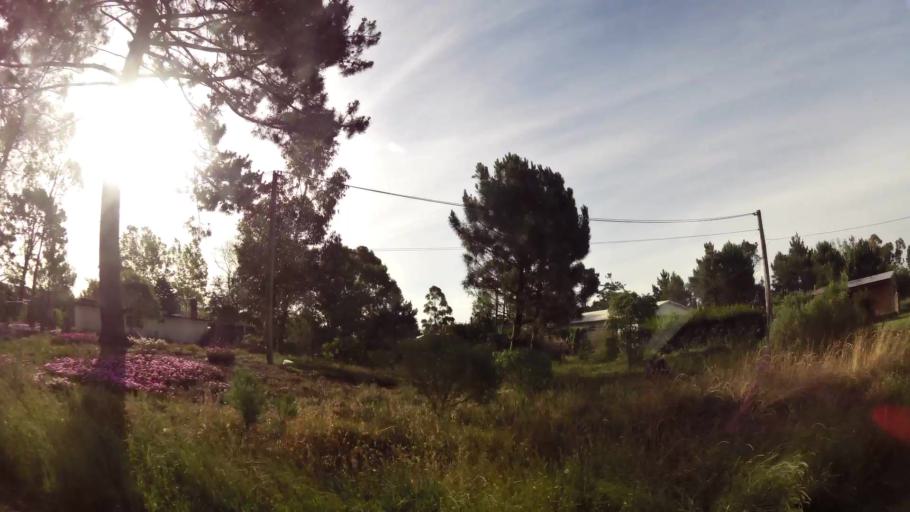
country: UY
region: Canelones
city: Empalme Olmos
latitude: -34.7826
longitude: -55.8586
